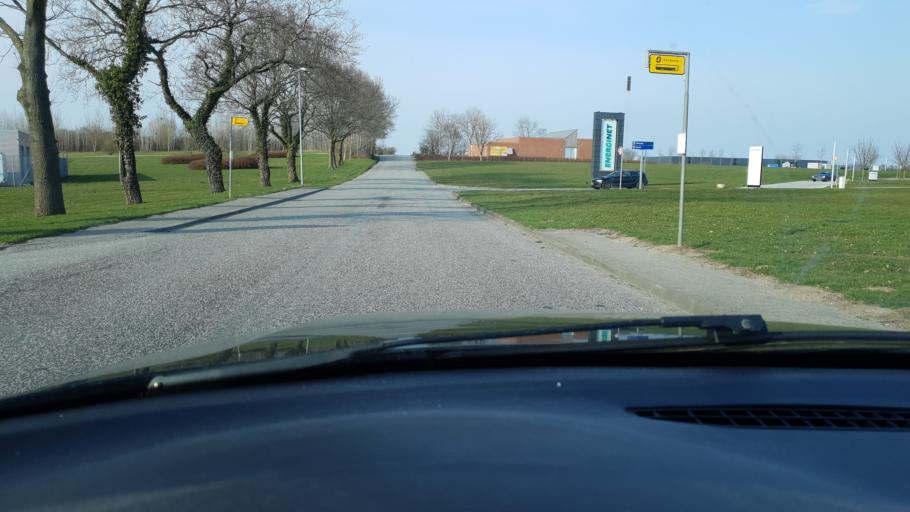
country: DK
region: South Denmark
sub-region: Fredericia Kommune
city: Snoghoj
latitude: 55.5345
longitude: 9.6971
